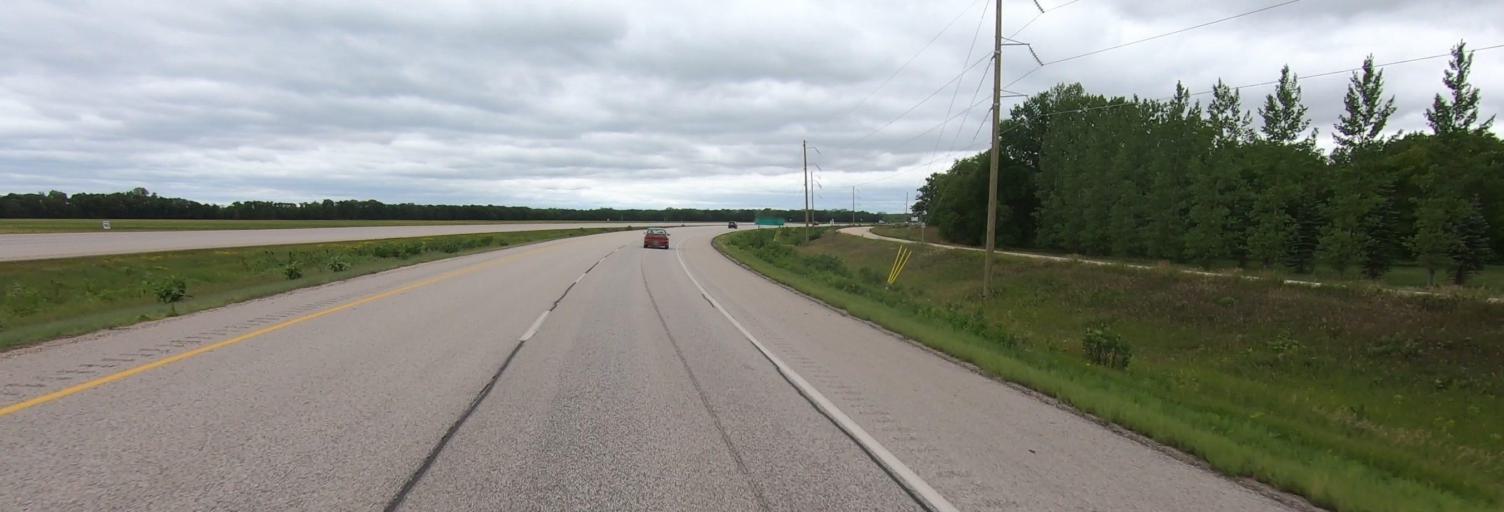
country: CA
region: Manitoba
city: Portage la Prairie
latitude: 49.9463
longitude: -98.2966
